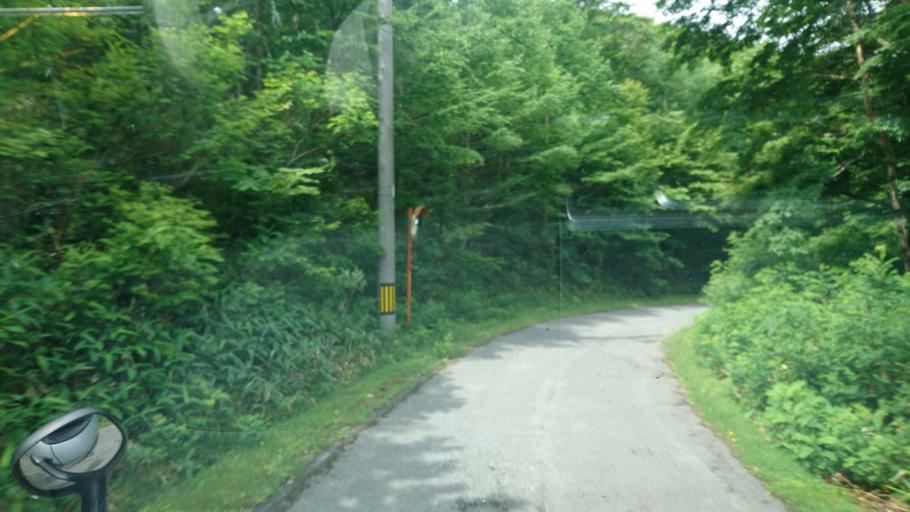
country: JP
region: Iwate
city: Ofunato
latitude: 39.1581
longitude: 141.7514
